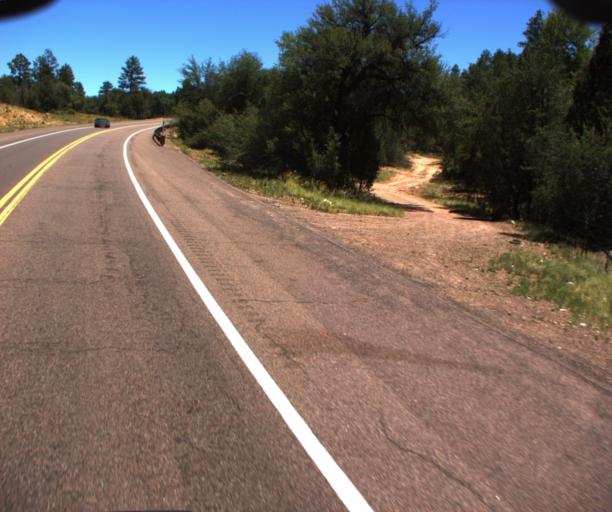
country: US
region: Arizona
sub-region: Gila County
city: Payson
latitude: 34.2793
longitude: -111.3250
